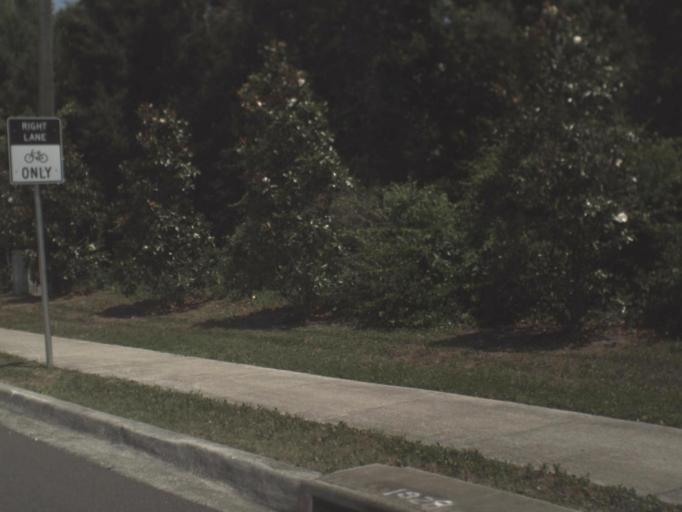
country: US
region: Florida
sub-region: Duval County
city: Jacksonville
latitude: 30.3534
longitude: -81.5413
